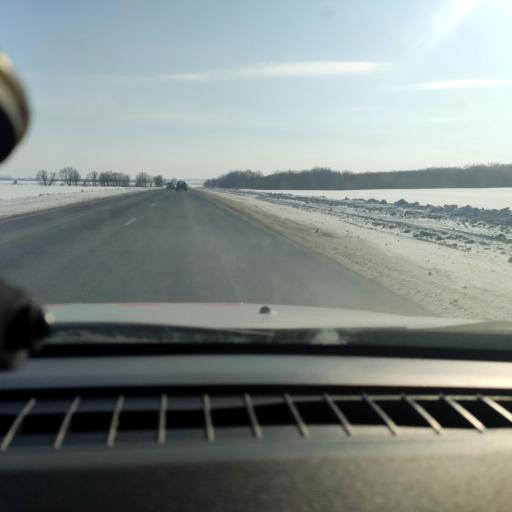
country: RU
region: Samara
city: Petra-Dubrava
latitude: 53.3266
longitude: 50.4545
